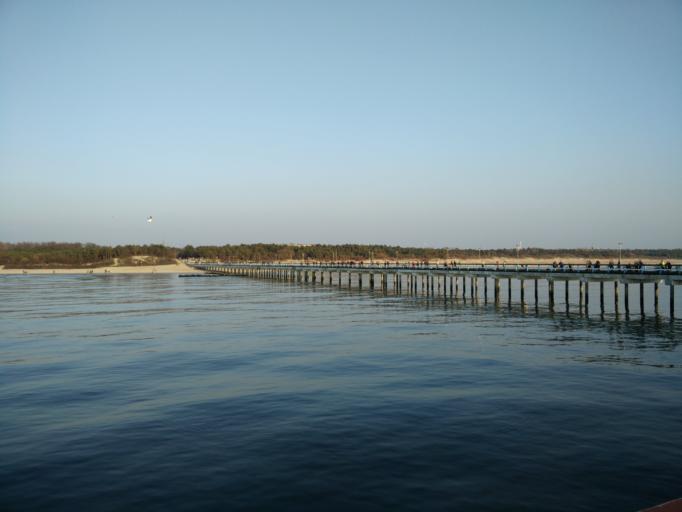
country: LT
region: Klaipedos apskritis
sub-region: Klaipeda
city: Palanga
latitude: 55.9210
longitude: 21.0446
